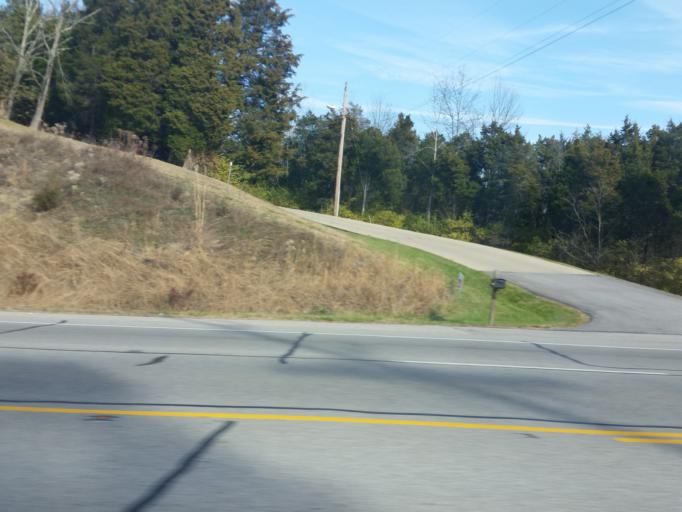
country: US
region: Kentucky
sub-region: Campbell County
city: Alexandria
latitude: 38.9881
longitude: -84.4057
